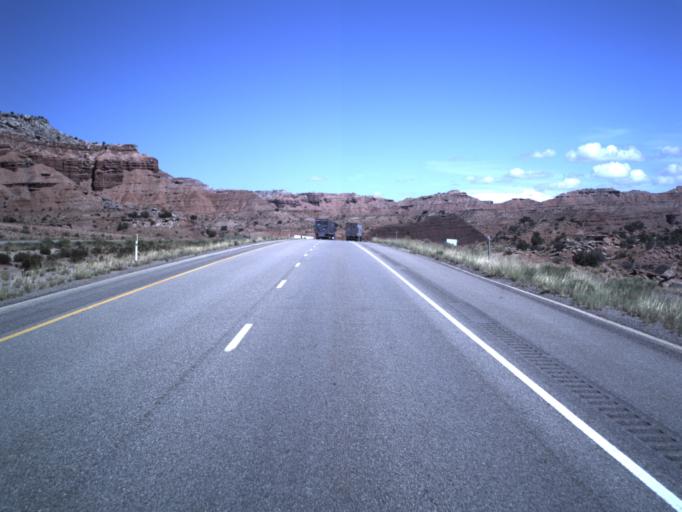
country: US
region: Utah
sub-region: Emery County
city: Ferron
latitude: 38.8294
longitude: -111.1381
